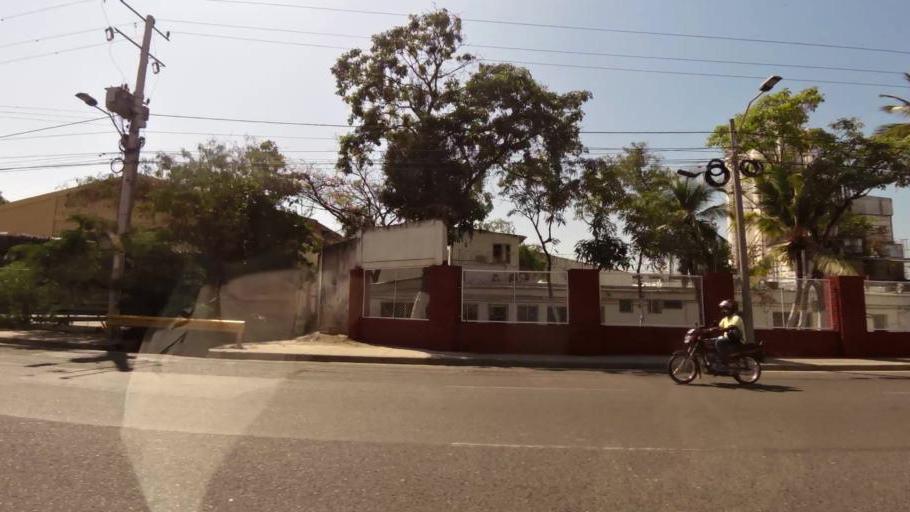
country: CO
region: Bolivar
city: Cartagena
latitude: 10.3885
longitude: -75.5149
